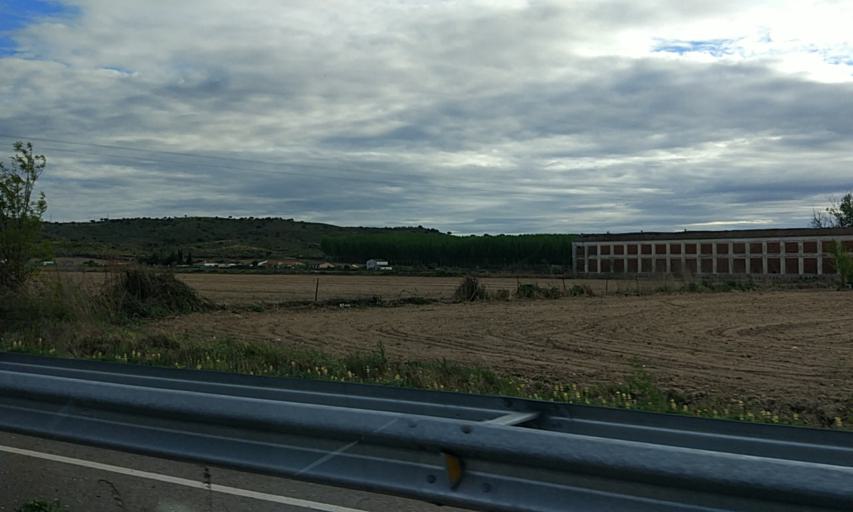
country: ES
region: Extremadura
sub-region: Provincia de Caceres
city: Coria
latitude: 39.9671
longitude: -6.5199
